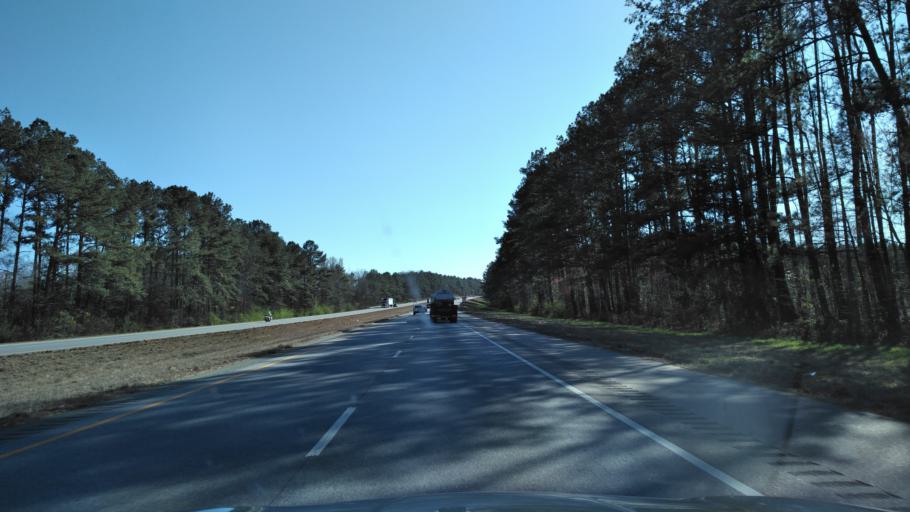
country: US
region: Alabama
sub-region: Butler County
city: Greenville
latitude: 31.7929
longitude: -86.6751
